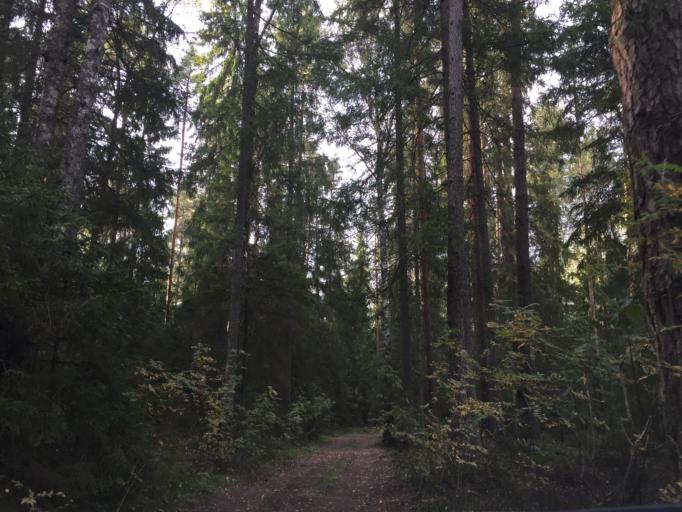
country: LV
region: Baldone
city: Baldone
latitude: 56.7840
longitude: 24.4416
